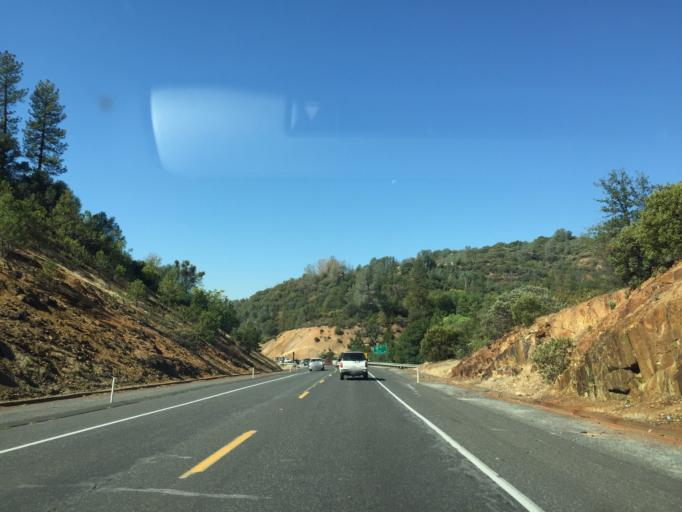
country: US
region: California
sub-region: Tuolumne County
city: Sonora
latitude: 37.9652
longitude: -120.3906
